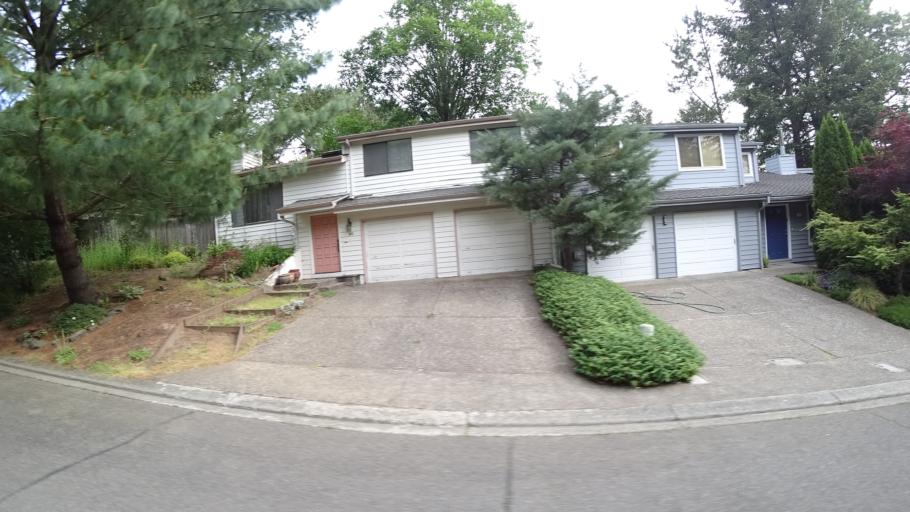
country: US
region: Oregon
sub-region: Clackamas County
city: Lake Oswego
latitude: 45.4259
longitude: -122.7094
